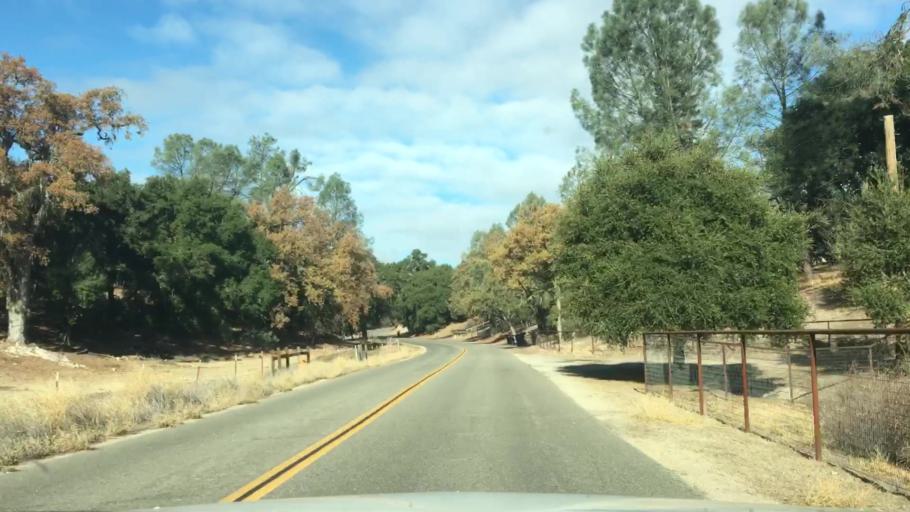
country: US
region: California
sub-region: San Luis Obispo County
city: Atascadero
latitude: 35.4502
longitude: -120.6518
